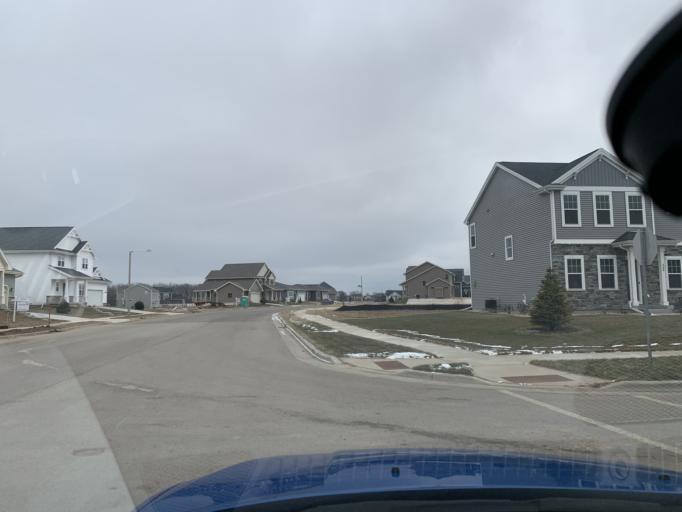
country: US
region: Wisconsin
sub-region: Dane County
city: Middleton
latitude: 43.0714
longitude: -89.5604
